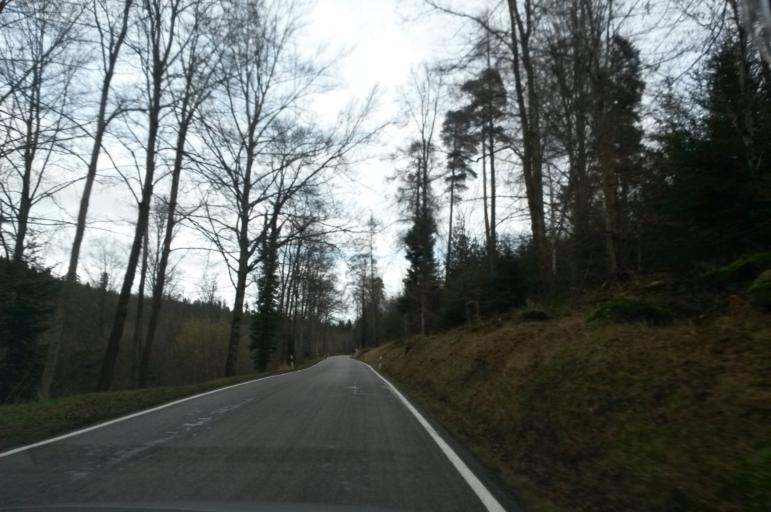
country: DE
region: Baden-Wuerttemberg
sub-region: Karlsruhe Region
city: Engelsbrand
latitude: 48.8370
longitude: 8.6299
